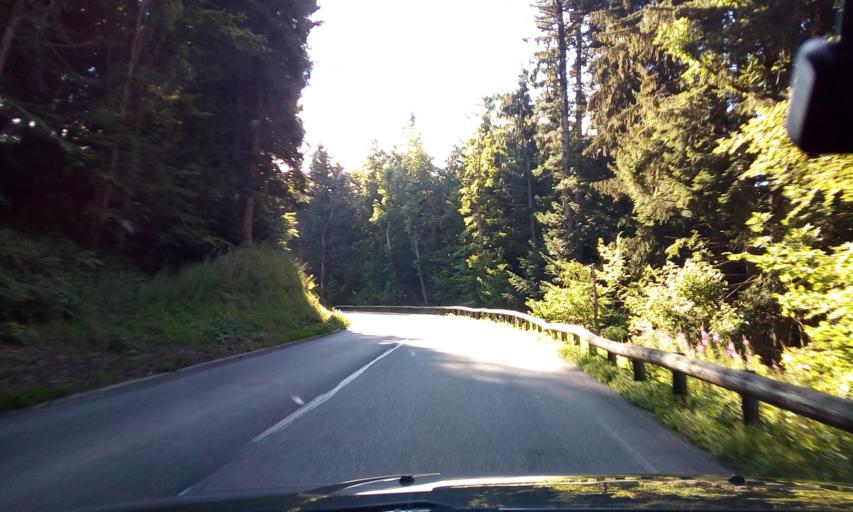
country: FR
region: Rhone-Alpes
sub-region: Departement de l'Isere
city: Sassenage
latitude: 45.1724
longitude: 5.6352
